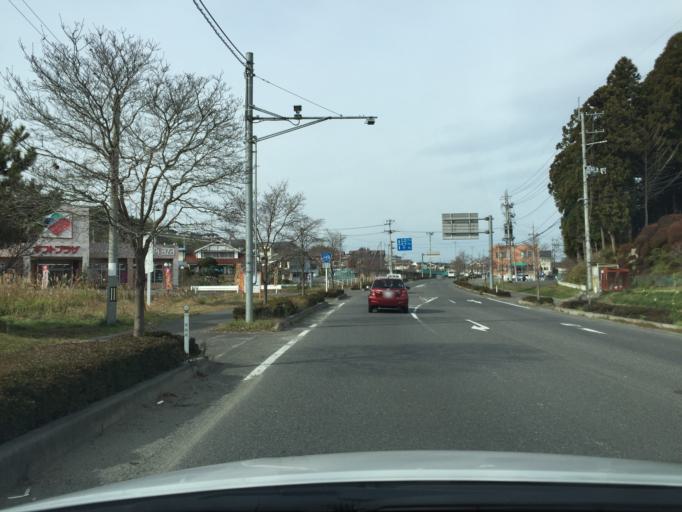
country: JP
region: Fukushima
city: Funehikimachi-funehiki
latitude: 37.4365
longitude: 140.5912
